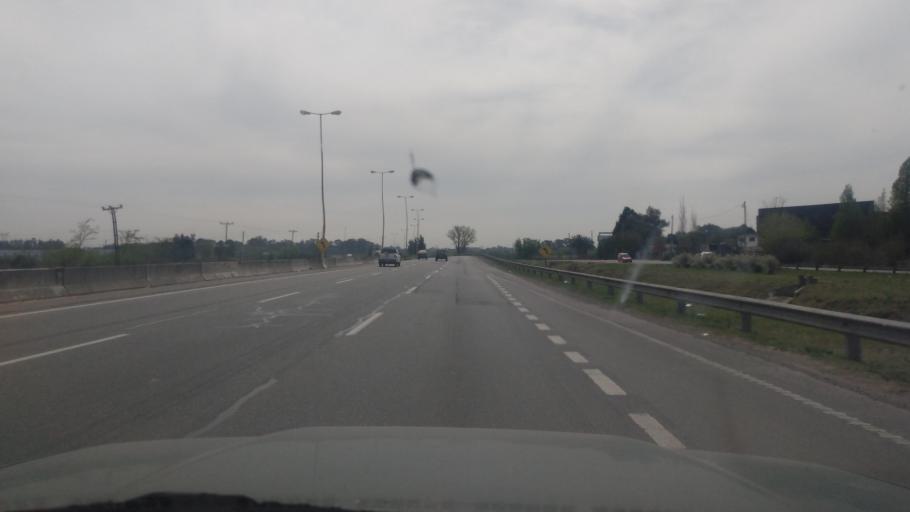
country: AR
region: Buenos Aires
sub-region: Partido de Pilar
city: Pilar
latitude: -34.4156
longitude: -59.0036
